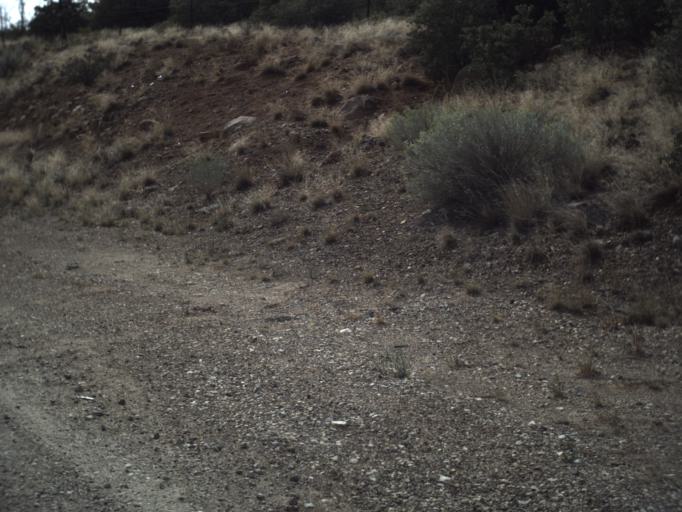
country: US
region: Utah
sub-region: Washington County
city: Toquerville
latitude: 37.3421
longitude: -113.2759
